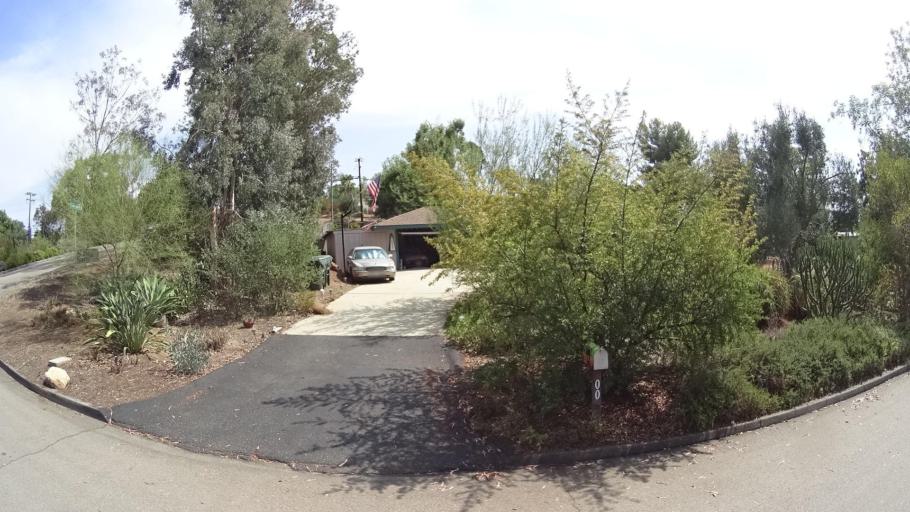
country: US
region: California
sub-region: San Diego County
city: Escondido
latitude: 33.0935
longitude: -117.0441
